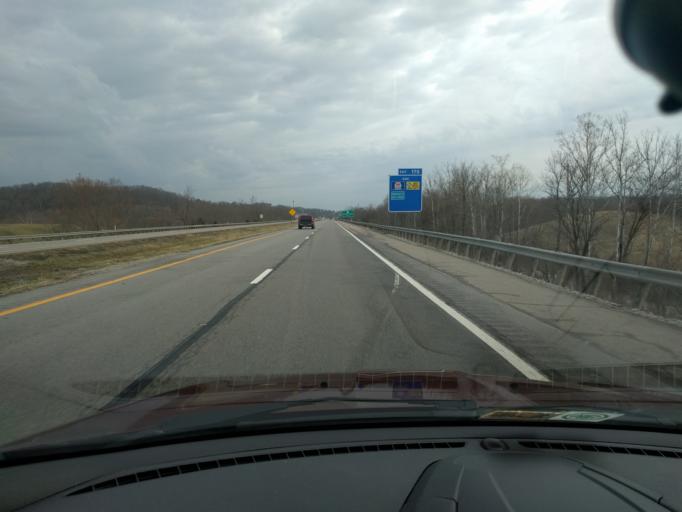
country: US
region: West Virginia
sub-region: Wood County
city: Mineral Wells
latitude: 39.1781
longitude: -81.5345
